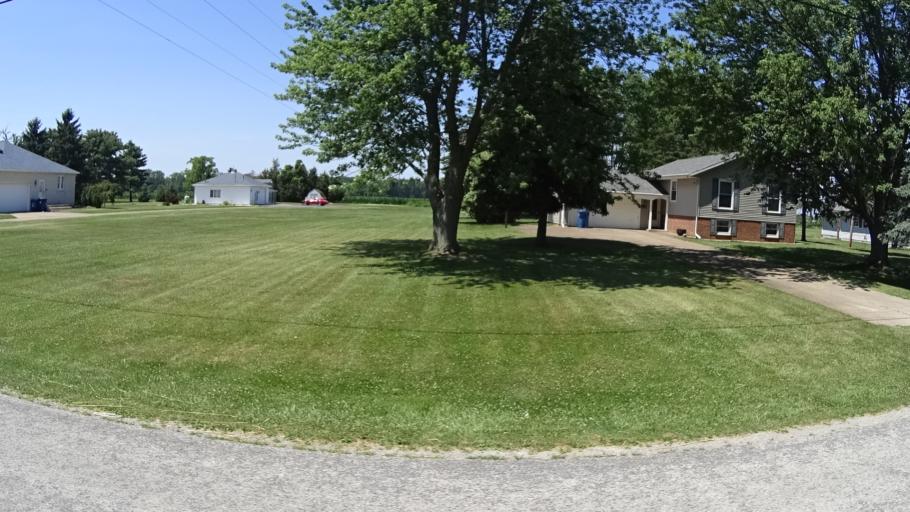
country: US
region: Ohio
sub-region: Erie County
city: Sandusky
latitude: 41.4352
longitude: -82.7927
